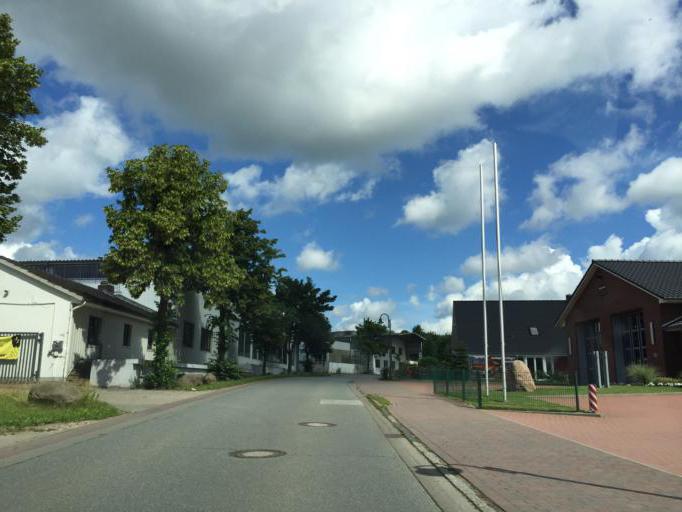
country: DE
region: Schleswig-Holstein
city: Scharbeutz
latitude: 54.0025
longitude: 10.7234
